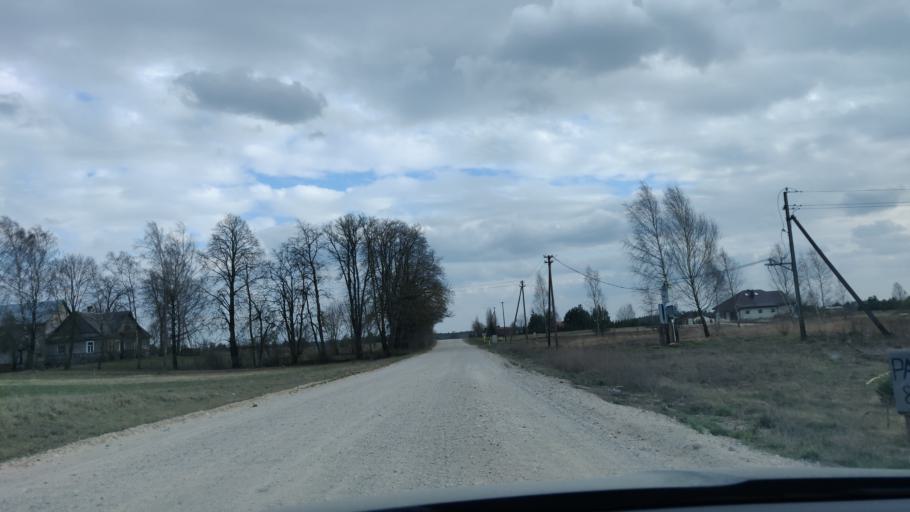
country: LT
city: Lentvaris
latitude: 54.6165
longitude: 25.0678
